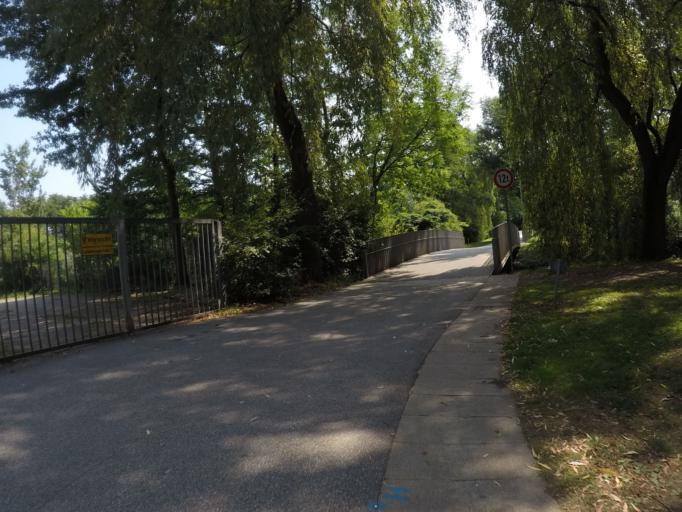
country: DE
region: Hamburg
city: Harburg
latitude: 53.4919
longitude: 9.9936
